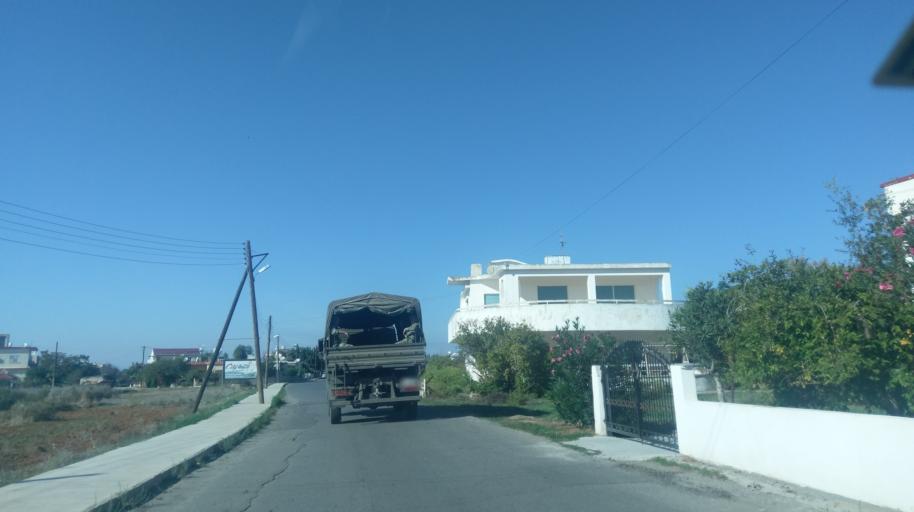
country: CY
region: Ammochostos
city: Famagusta
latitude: 35.1010
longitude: 33.9486
